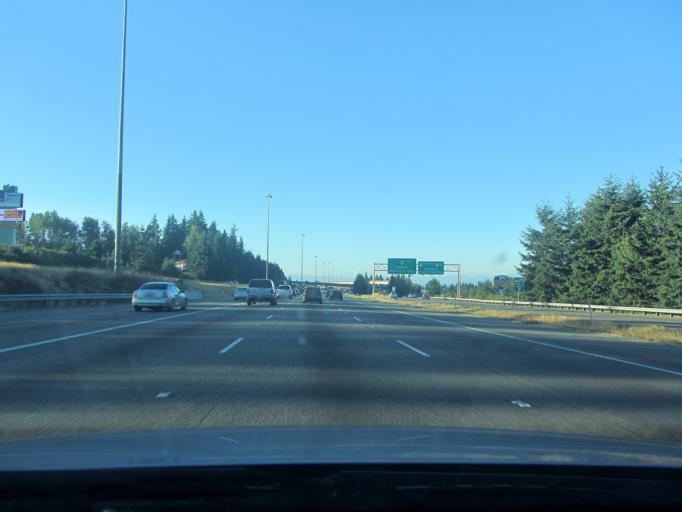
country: US
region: Washington
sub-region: Snohomish County
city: Mill Creek
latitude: 47.9099
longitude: -122.2101
